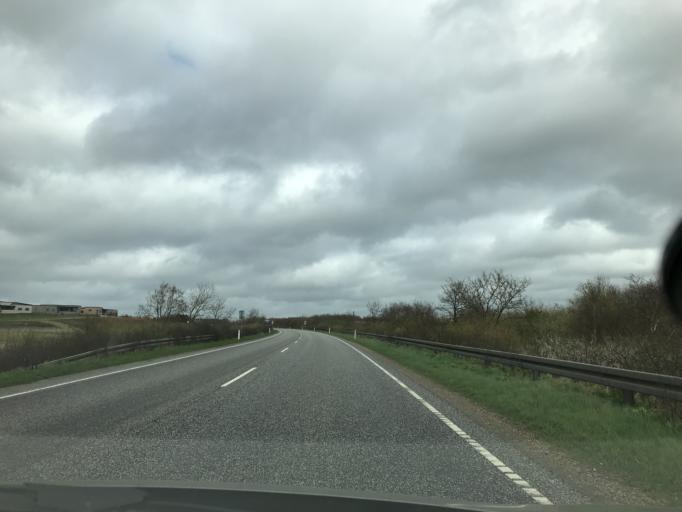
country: DK
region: Central Jutland
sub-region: Skive Kommune
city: Skive
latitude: 56.5764
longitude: 9.0160
